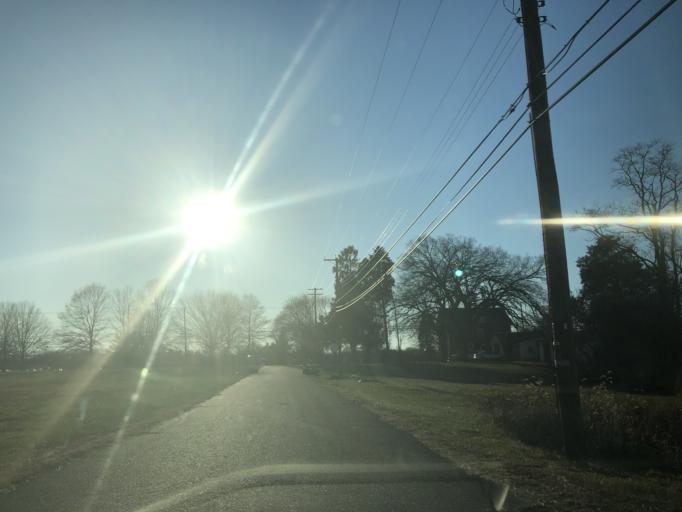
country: US
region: New Jersey
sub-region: Salem County
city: Carneys Point
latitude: 39.7071
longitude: -75.4430
